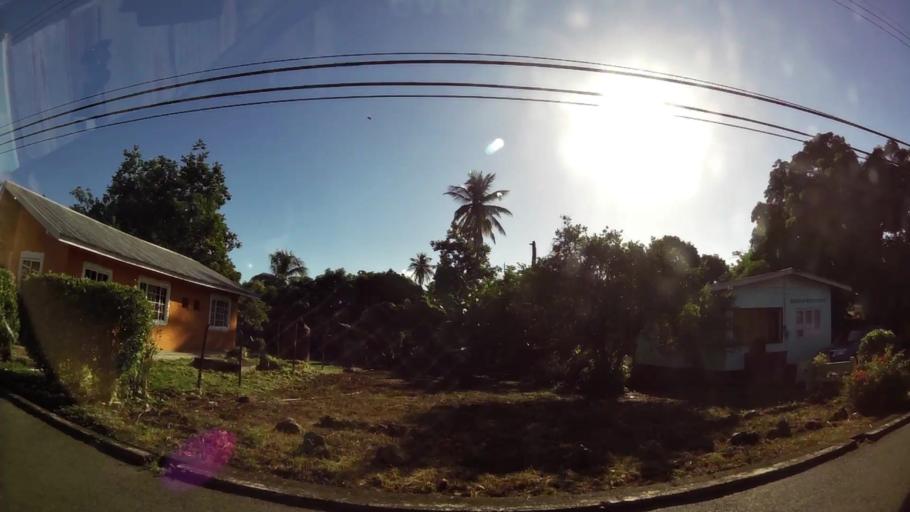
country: TT
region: Tobago
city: Scarborough
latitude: 11.1559
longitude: -60.8234
